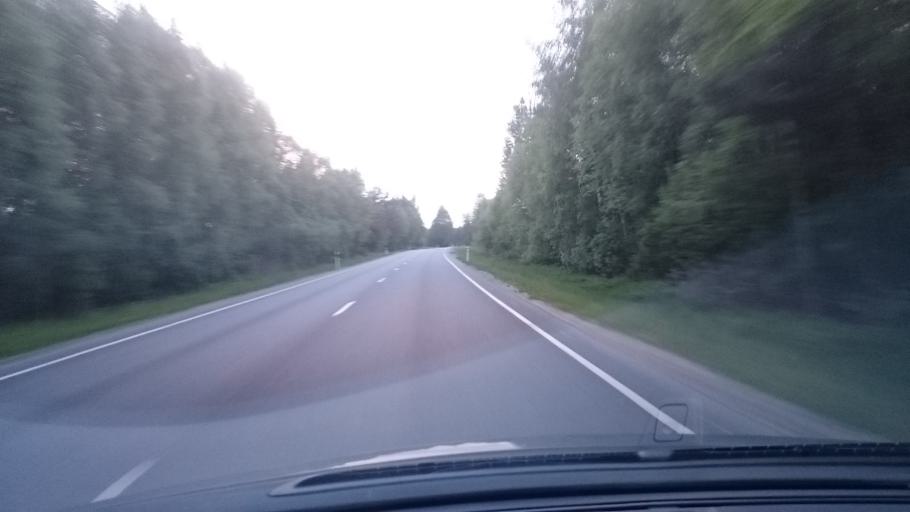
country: EE
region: Raplamaa
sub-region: Kehtna vald
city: Kehtna
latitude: 58.8678
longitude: 24.9886
